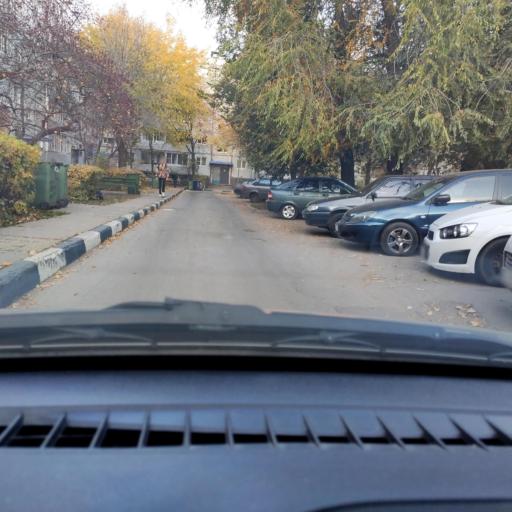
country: RU
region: Samara
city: Tol'yatti
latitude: 53.5311
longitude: 49.3000
